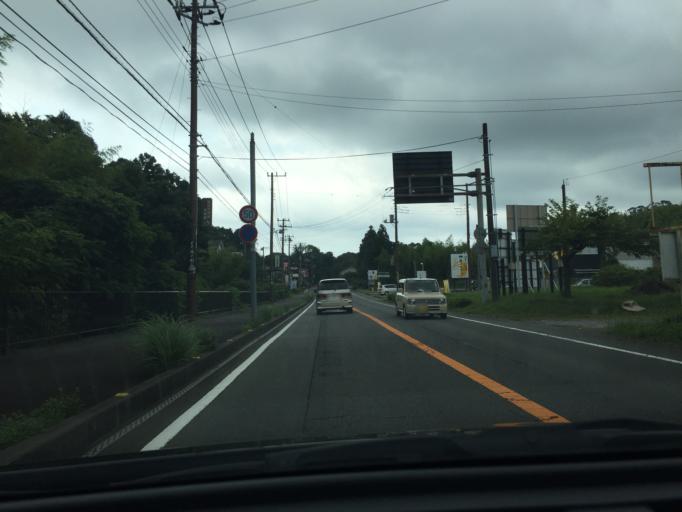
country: JP
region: Shizuoka
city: Ito
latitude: 34.9206
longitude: 139.1196
